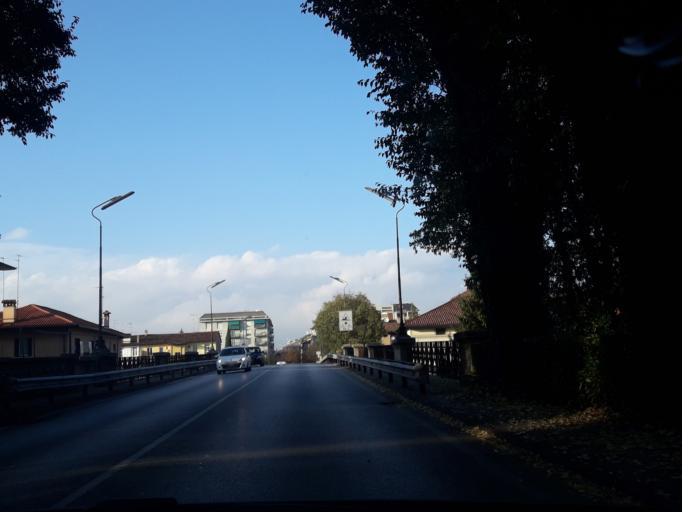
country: IT
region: Friuli Venezia Giulia
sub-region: Provincia di Udine
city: Udine
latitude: 46.0558
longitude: 13.2467
